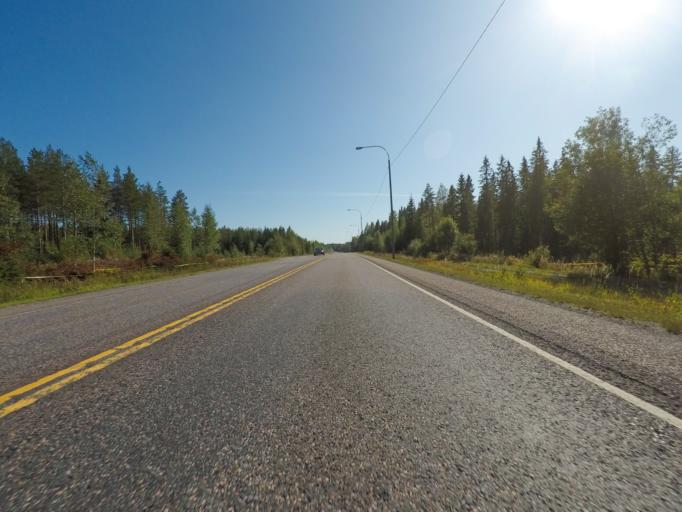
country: FI
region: Northern Savo
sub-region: Varkaus
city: Varkaus
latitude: 62.3691
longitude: 27.8097
